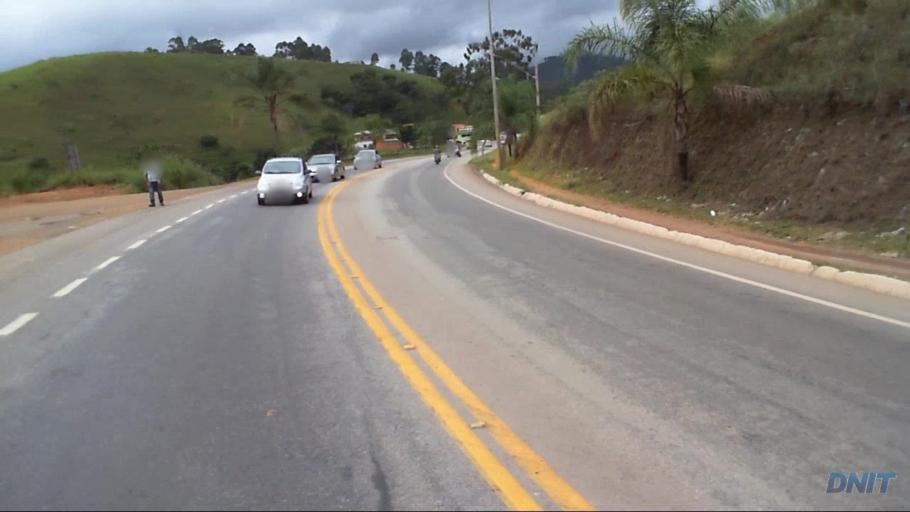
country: BR
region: Minas Gerais
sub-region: Joao Monlevade
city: Joao Monlevade
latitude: -19.8374
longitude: -43.1890
